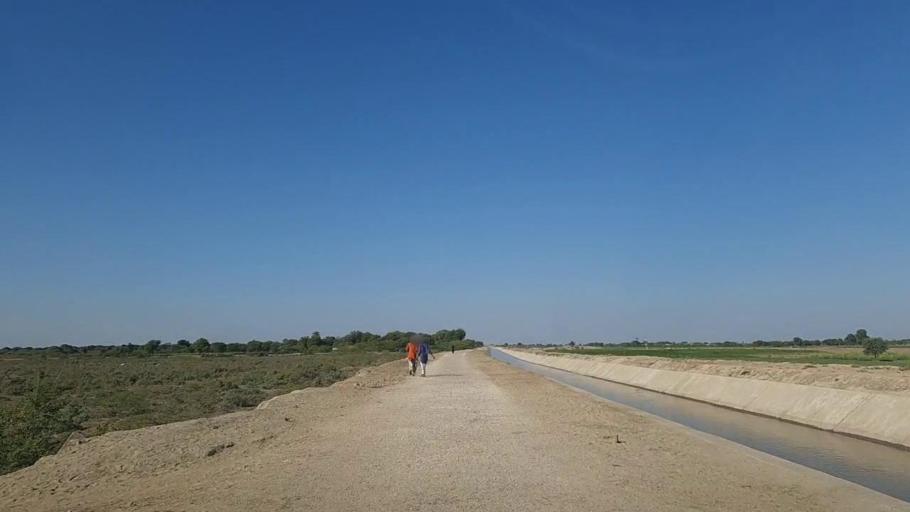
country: PK
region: Sindh
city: Kunri
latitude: 25.2270
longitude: 69.5149
